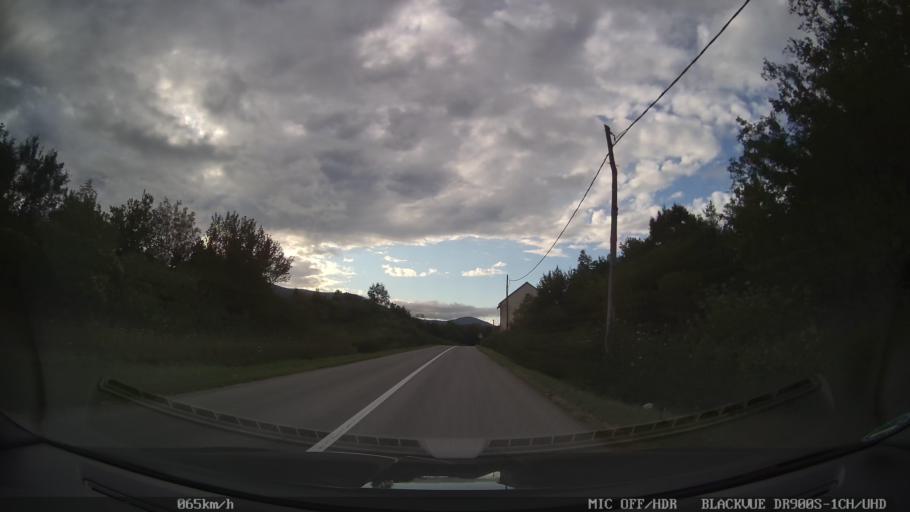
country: HR
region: Karlovacka
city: Plaski
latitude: 44.9943
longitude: 15.4456
